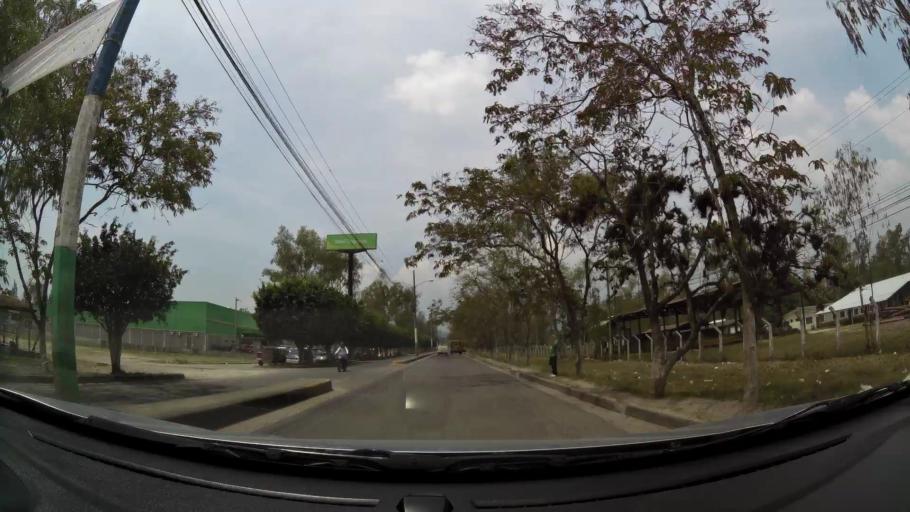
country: HN
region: Comayagua
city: Siguatepeque
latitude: 14.5839
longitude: -87.8351
